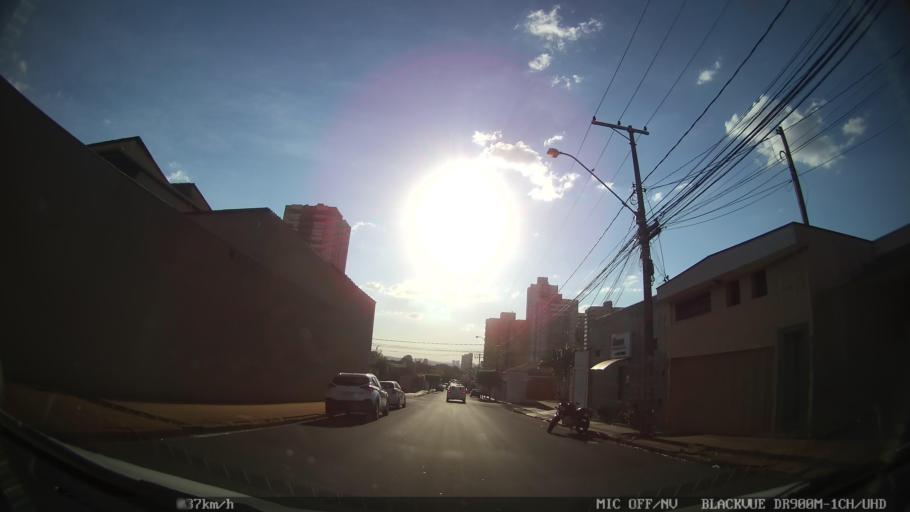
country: BR
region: Sao Paulo
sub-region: Ribeirao Preto
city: Ribeirao Preto
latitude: -21.1834
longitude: -47.7901
